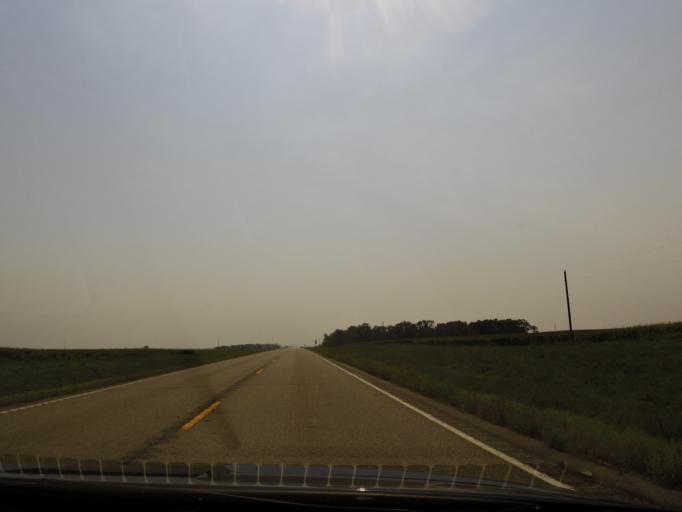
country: US
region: South Dakota
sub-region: Roberts County
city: Sisseton
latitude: 45.9961
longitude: -97.1156
